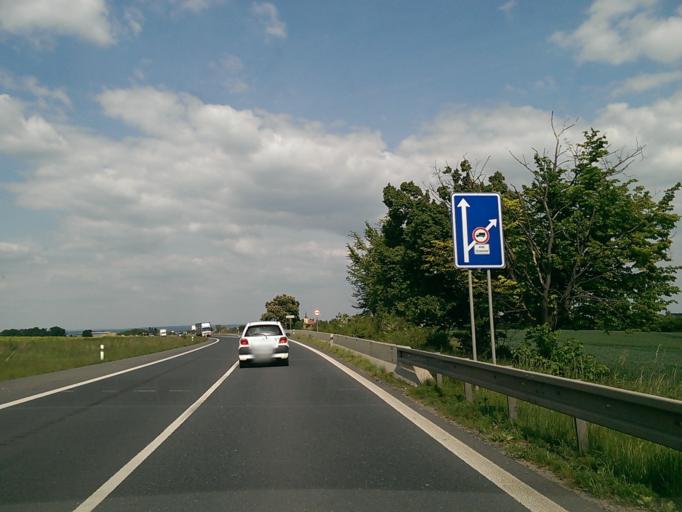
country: CZ
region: Central Bohemia
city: Libeznice
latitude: 50.1860
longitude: 14.4786
